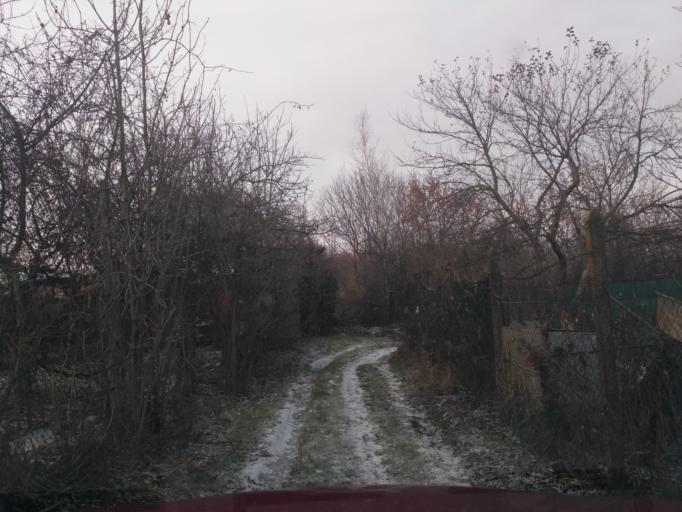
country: SK
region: Kosicky
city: Kosice
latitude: 48.7293
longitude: 21.2704
